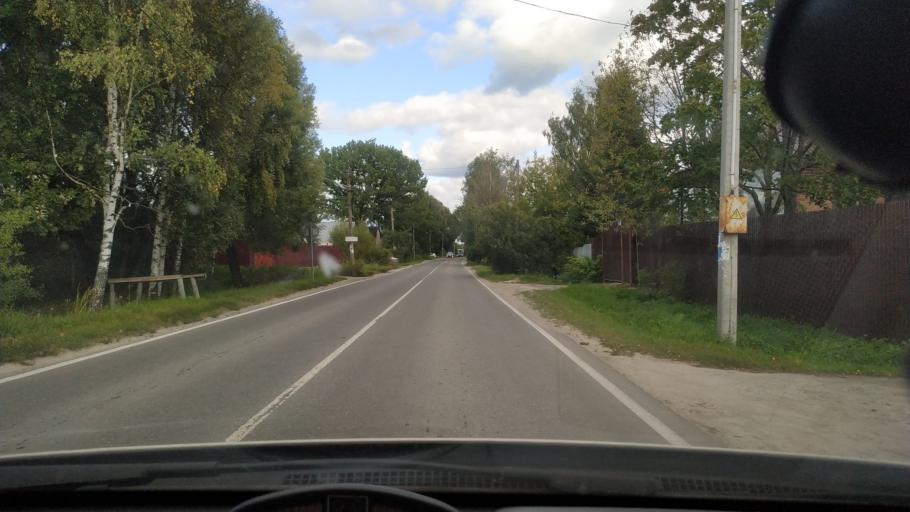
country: RU
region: Moskovskaya
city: Fryazevo
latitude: 55.7231
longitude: 38.4330
